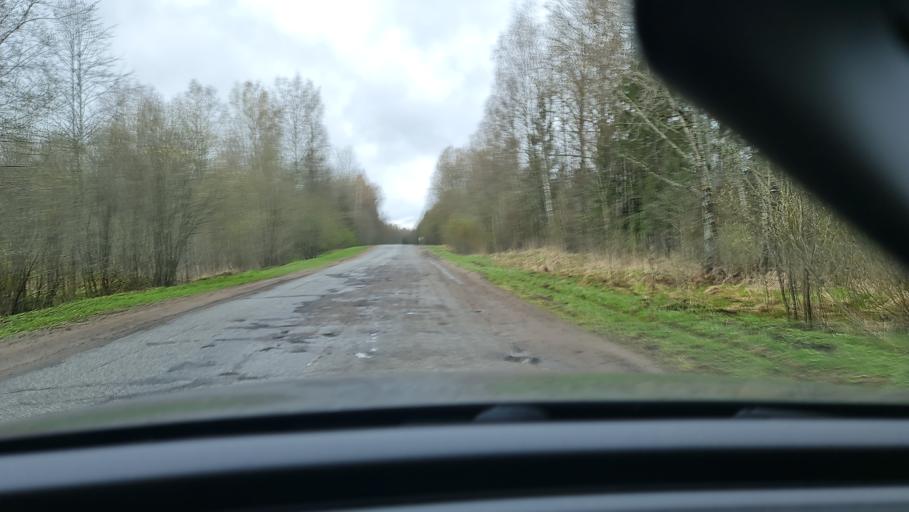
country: RU
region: Novgorod
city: Marevo
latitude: 57.2674
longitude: 32.0805
